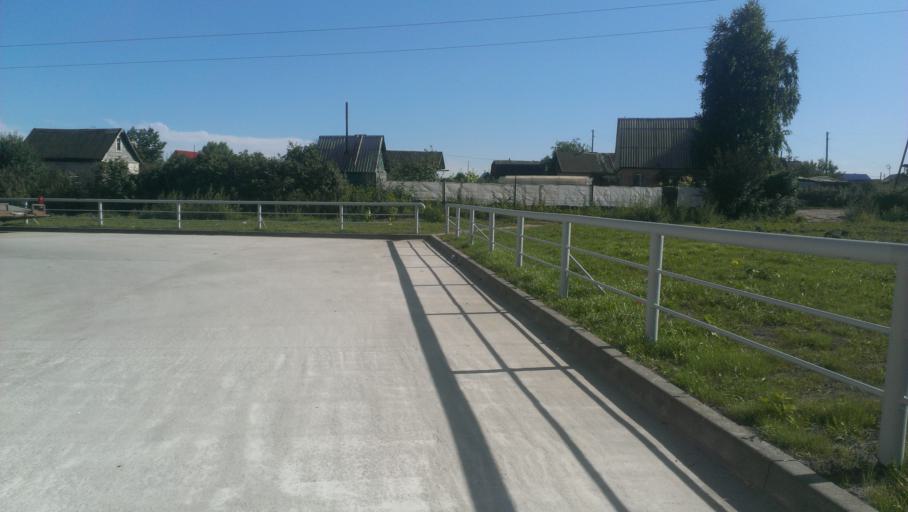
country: RU
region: Altai Krai
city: Novosilikatnyy
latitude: 53.3262
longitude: 83.6674
